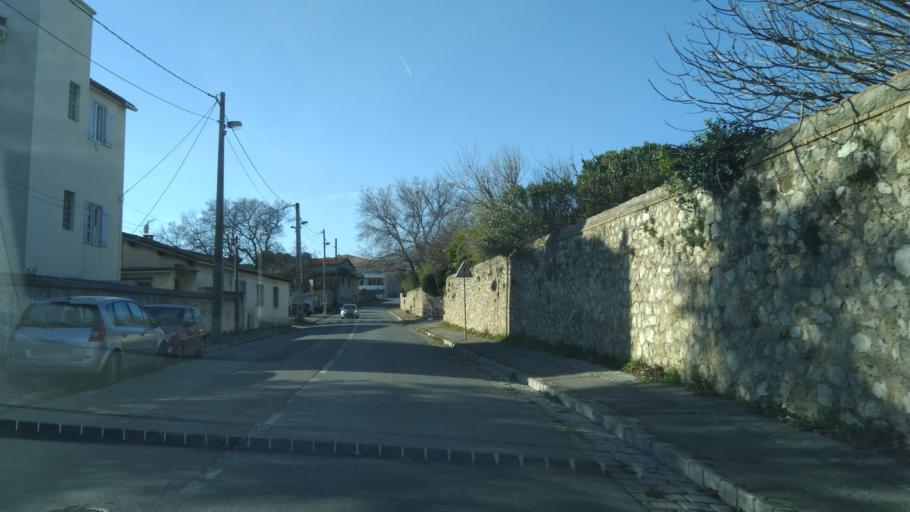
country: FR
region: Provence-Alpes-Cote d'Azur
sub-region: Departement des Bouches-du-Rhone
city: Marseille 12
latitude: 43.3028
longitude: 5.4462
